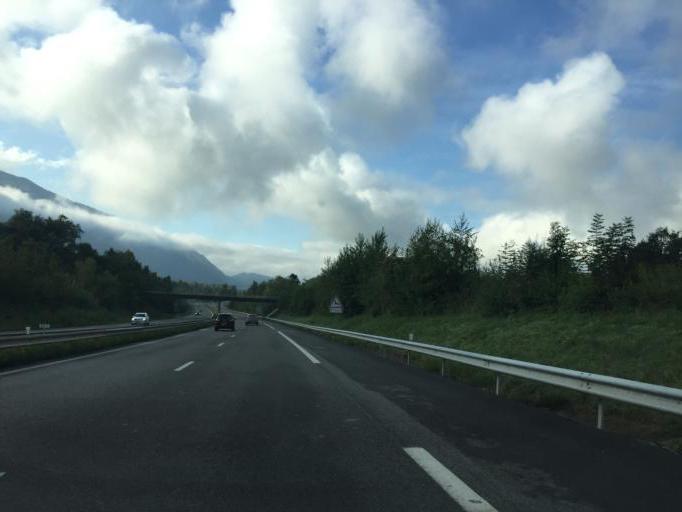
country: FR
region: Rhone-Alpes
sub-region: Departement de la Savoie
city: Drumettaz-Clarafond
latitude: 45.6660
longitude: 5.9250
